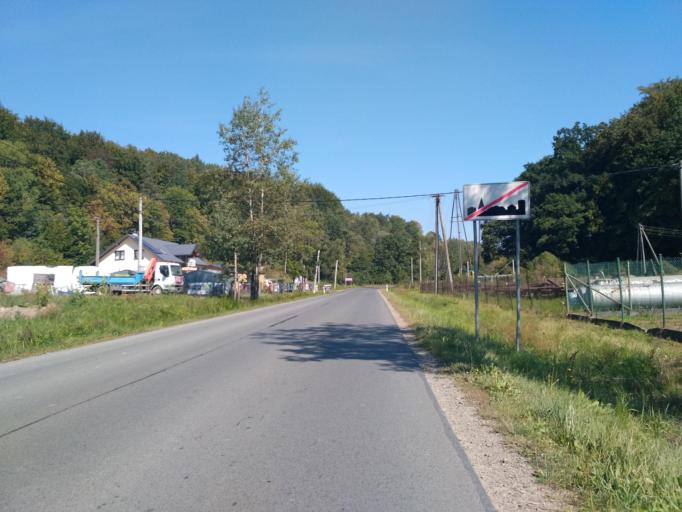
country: PL
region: Subcarpathian Voivodeship
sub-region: Powiat brzozowski
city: Grabownica Starzenska
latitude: 49.6681
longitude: 22.0835
